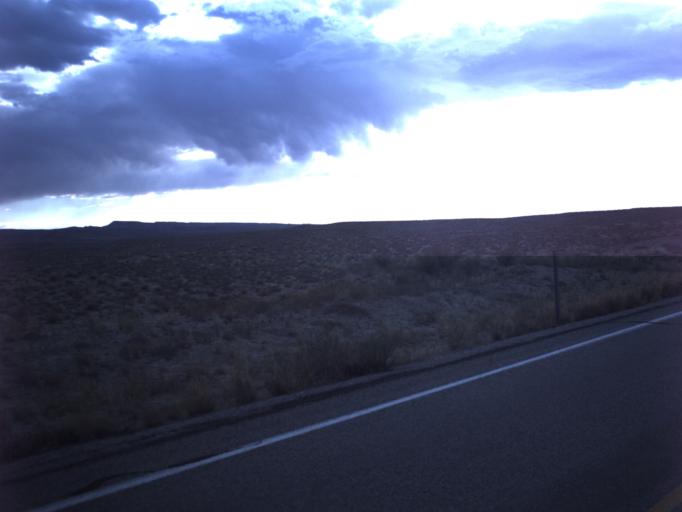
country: US
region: Utah
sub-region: Grand County
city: Moab
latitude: 38.9045
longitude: -109.3212
